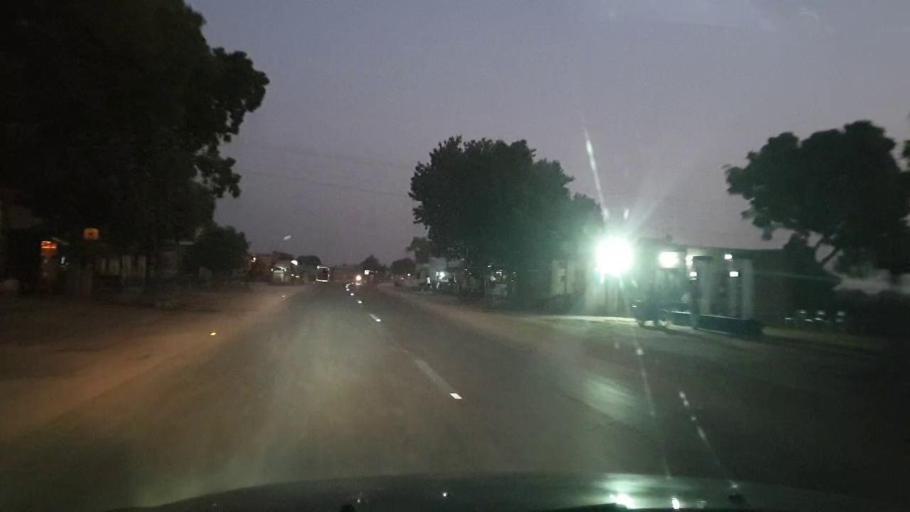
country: PK
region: Sindh
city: Chambar
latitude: 25.3816
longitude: 68.7758
